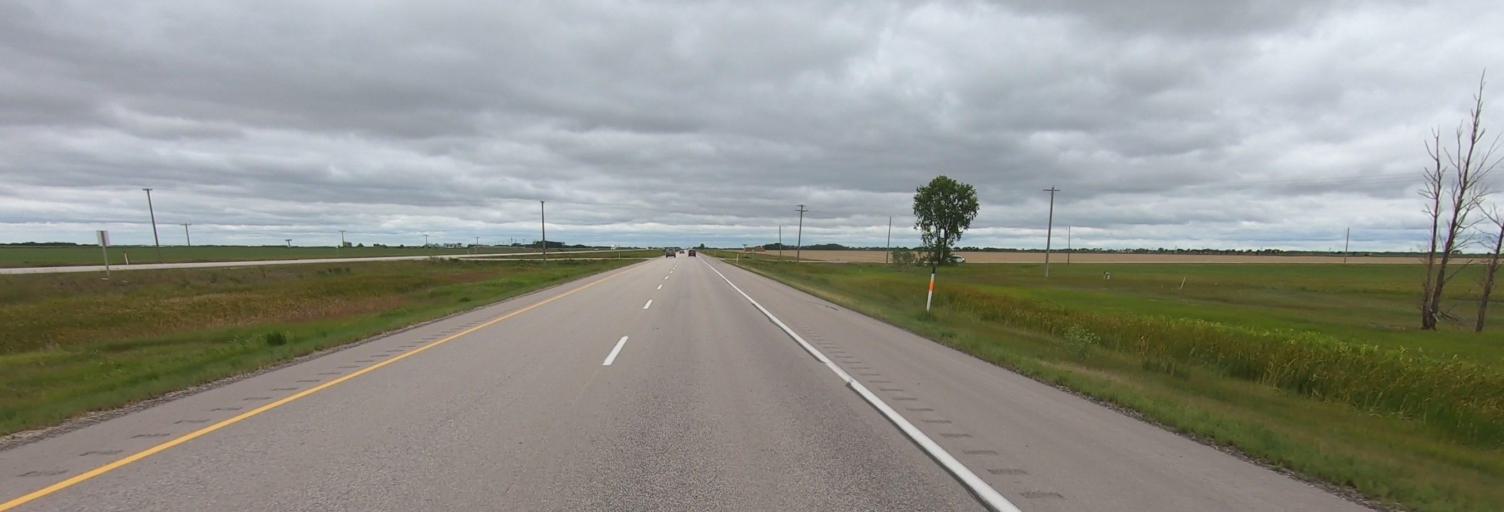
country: CA
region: Manitoba
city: Headingley
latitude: 49.9152
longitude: -97.8014
